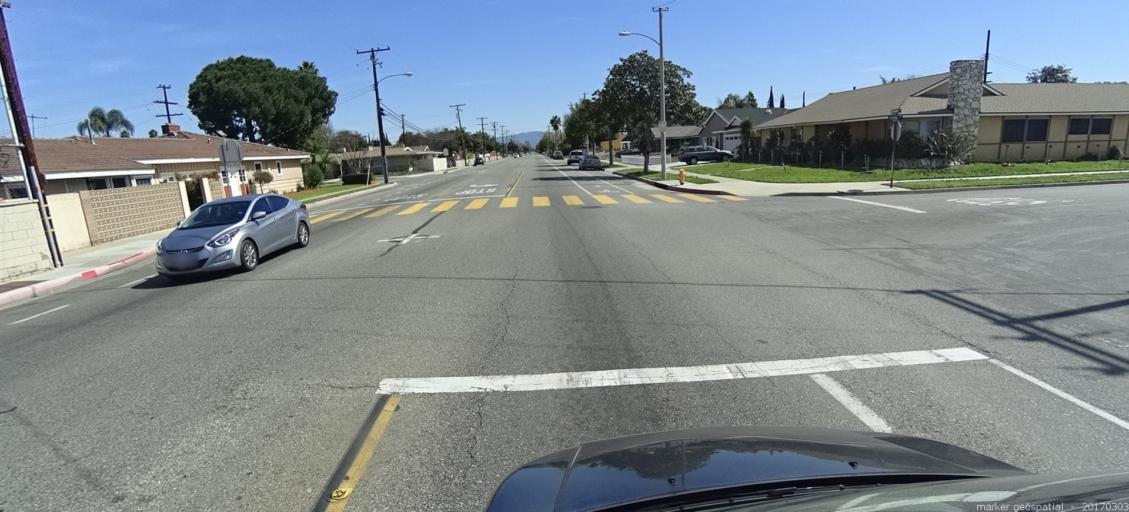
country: US
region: California
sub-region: Orange County
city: Garden Grove
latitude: 33.7959
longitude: -117.9371
